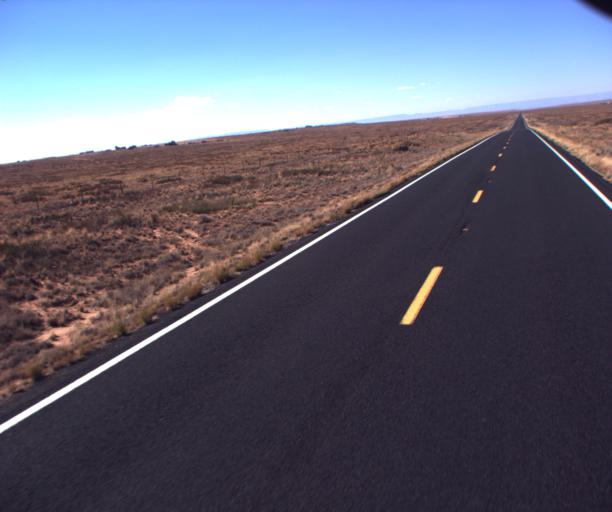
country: US
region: Arizona
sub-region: Coconino County
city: Tuba City
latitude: 36.0126
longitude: -111.0794
